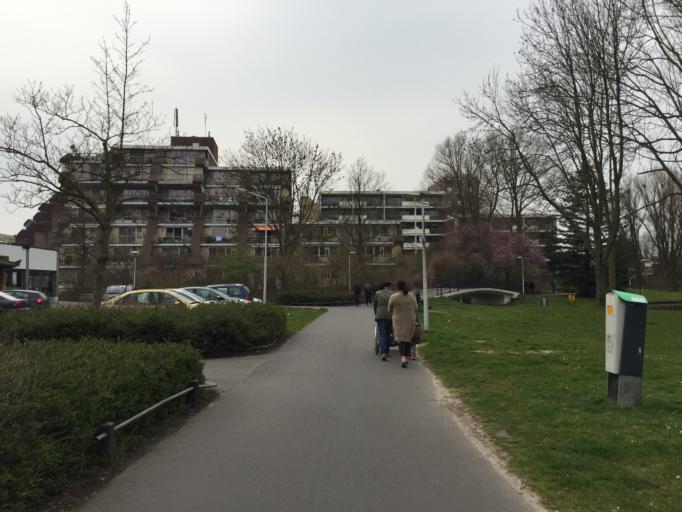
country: NL
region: South Holland
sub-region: Gemeente Leiden
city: Leiden
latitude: 52.1772
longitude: 4.5061
